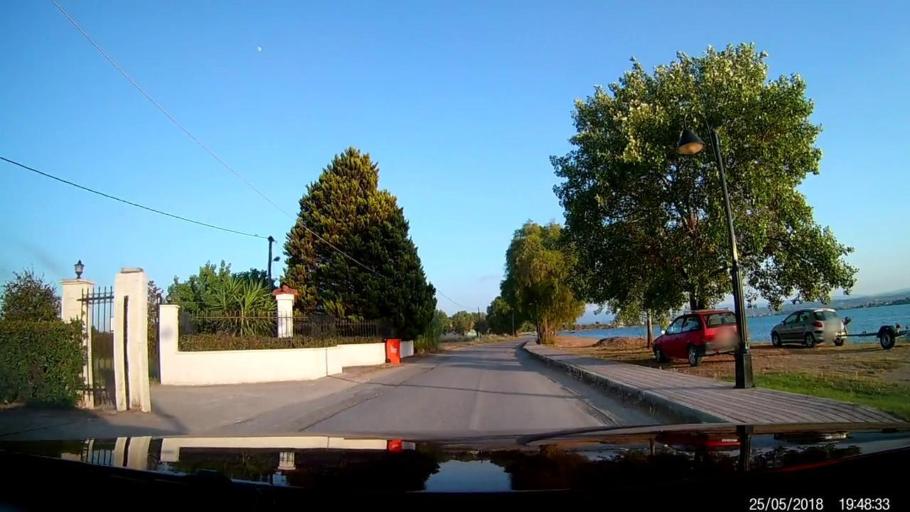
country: GR
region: Central Greece
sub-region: Nomos Evvoias
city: Ayios Nikolaos
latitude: 38.4166
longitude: 23.6393
